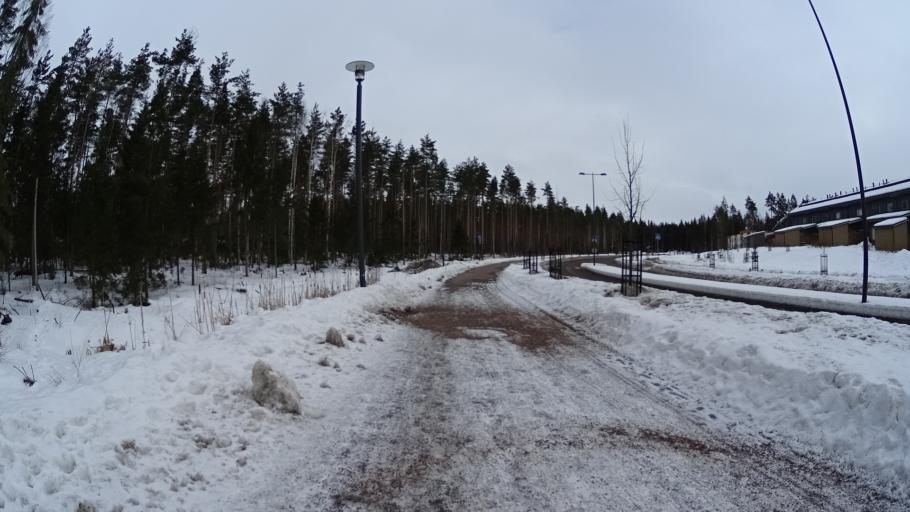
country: FI
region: Uusimaa
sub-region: Helsinki
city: Kilo
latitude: 60.2420
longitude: 24.8183
